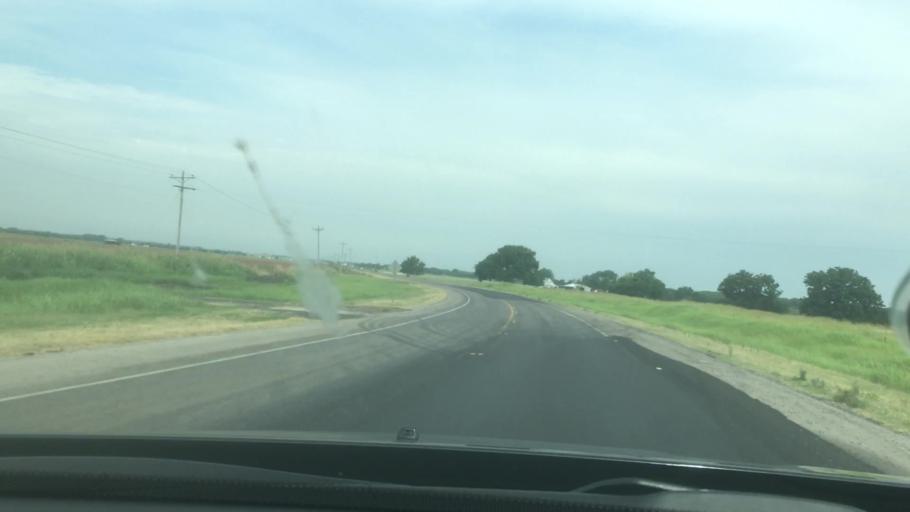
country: US
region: Oklahoma
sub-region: Garvin County
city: Maysville
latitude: 34.8211
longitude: -97.4944
